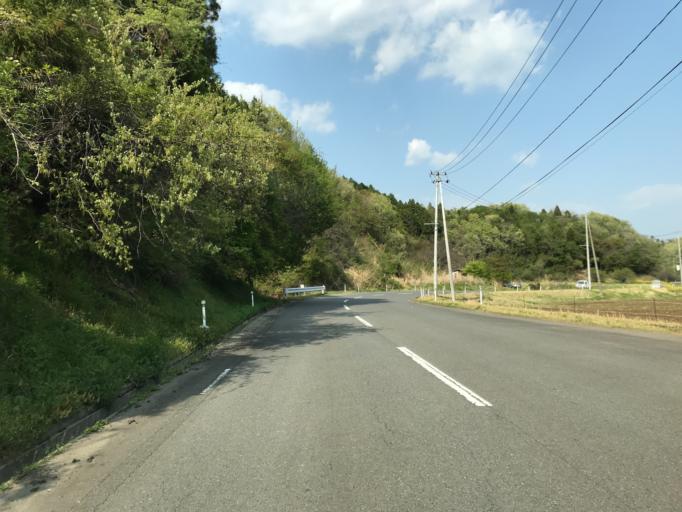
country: JP
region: Fukushima
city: Iwaki
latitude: 36.9952
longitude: 140.7693
